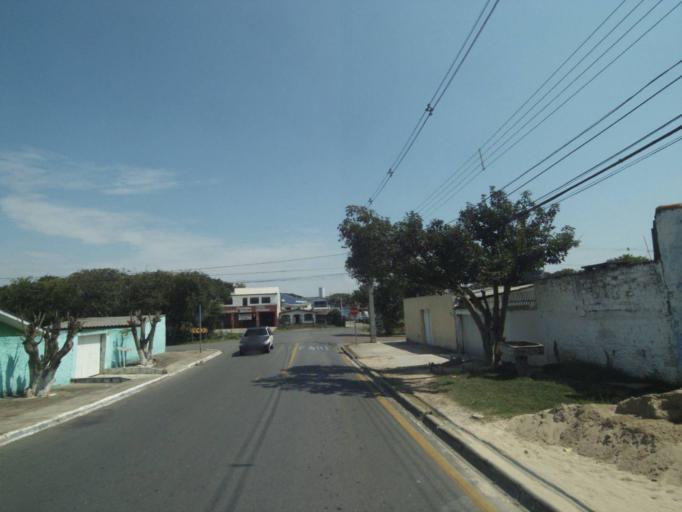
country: BR
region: Parana
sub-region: Curitiba
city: Curitiba
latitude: -25.4780
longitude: -49.3181
